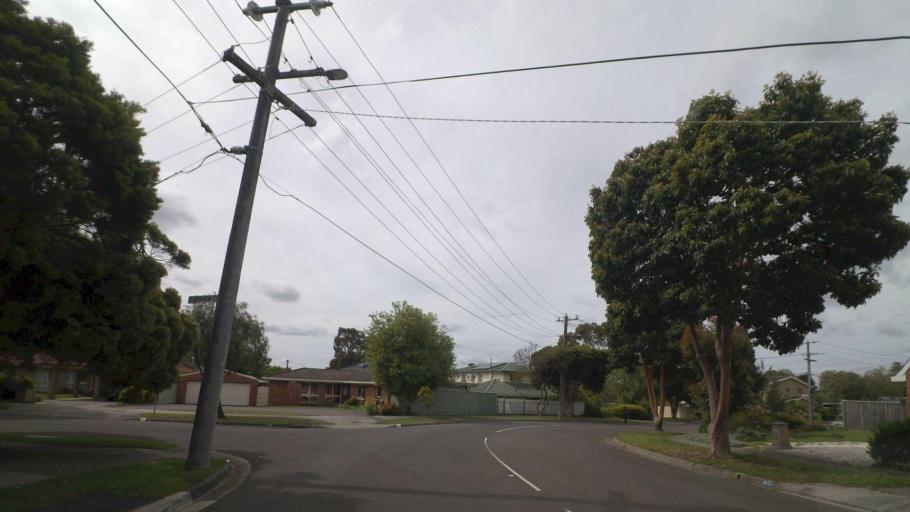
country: AU
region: Victoria
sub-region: Knox
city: Knoxfield
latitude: -37.8836
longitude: 145.2535
